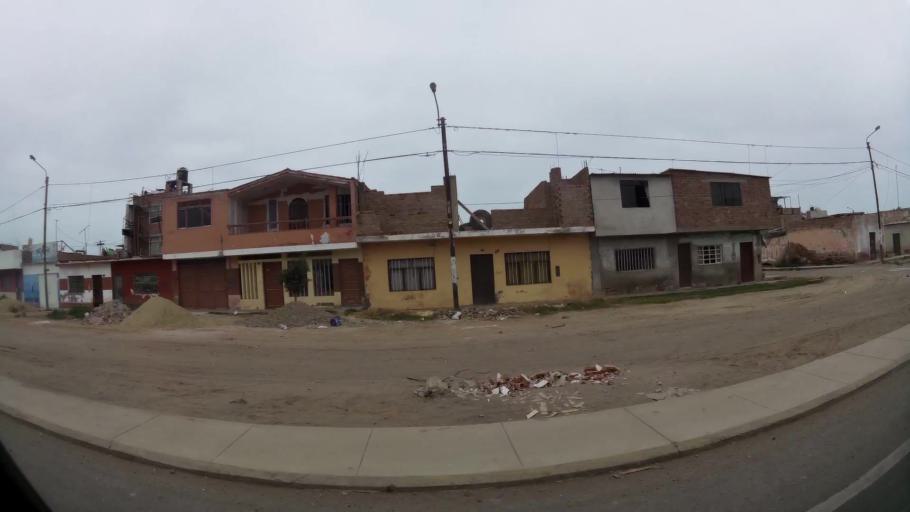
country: PE
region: La Libertad
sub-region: Provincia de Trujillo
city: Buenos Aires
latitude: -8.1418
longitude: -79.0512
